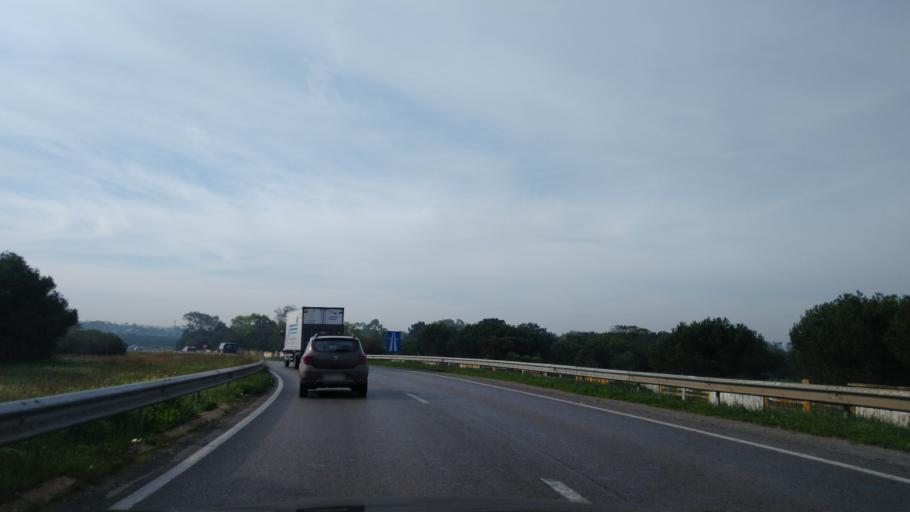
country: MA
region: Rabat-Sale-Zemmour-Zaer
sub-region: Skhirate-Temara
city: Temara
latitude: 33.9495
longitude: -6.9203
